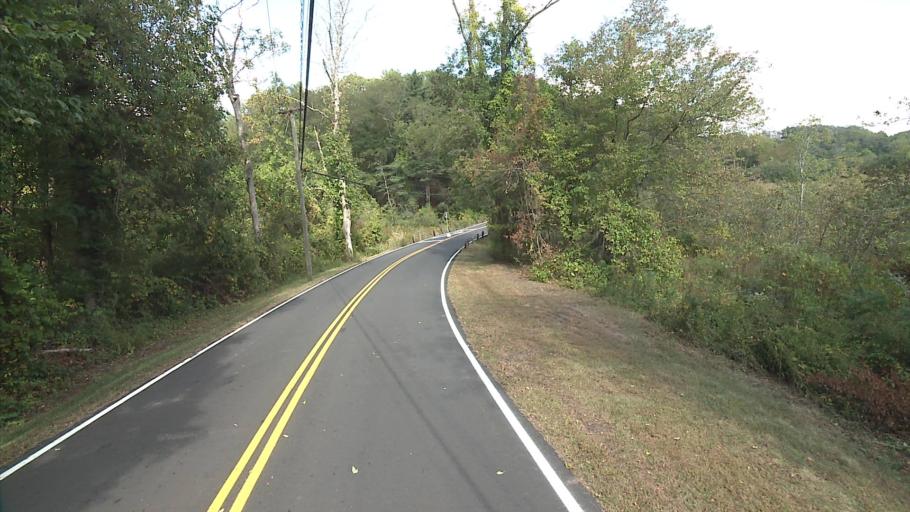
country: US
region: Connecticut
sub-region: Middlesex County
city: Chester Center
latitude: 41.4177
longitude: -72.4366
